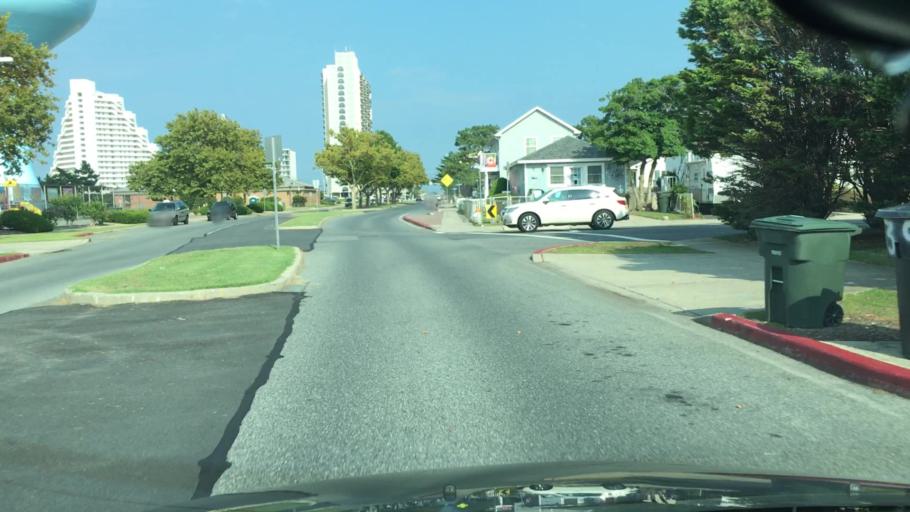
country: US
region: Maryland
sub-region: Worcester County
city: Ocean City
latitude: 38.4096
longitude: -75.0628
